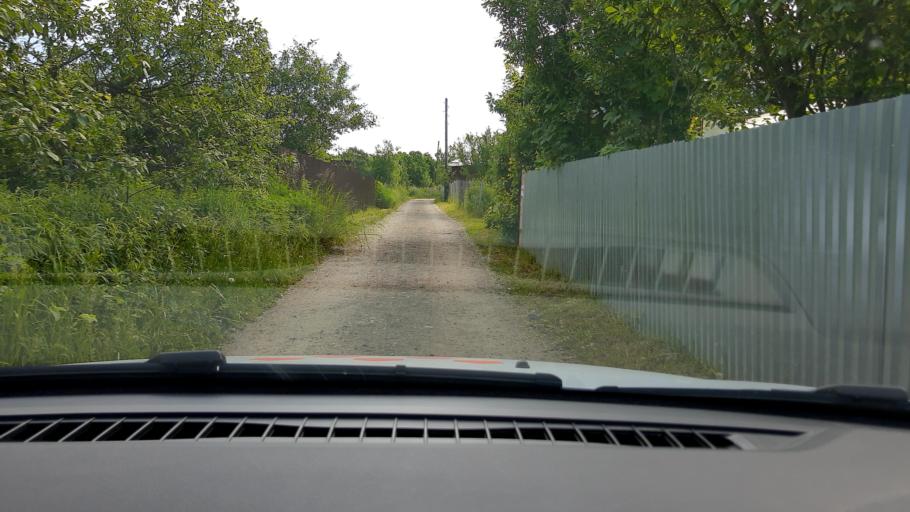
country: RU
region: Nizjnij Novgorod
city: Linda
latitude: 56.6610
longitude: 44.1705
